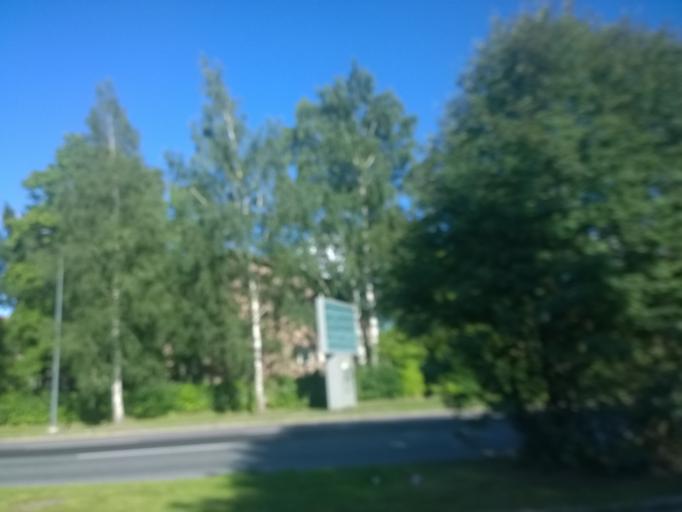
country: FI
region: Pirkanmaa
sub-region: Tampere
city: Tampere
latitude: 61.4864
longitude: 23.7781
